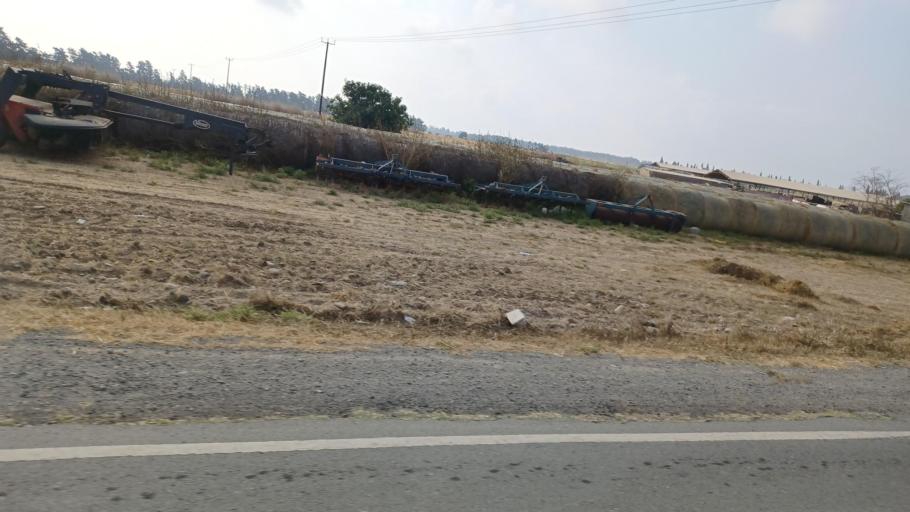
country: CY
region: Larnaka
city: Meneou
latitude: 34.8514
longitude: 33.5950
